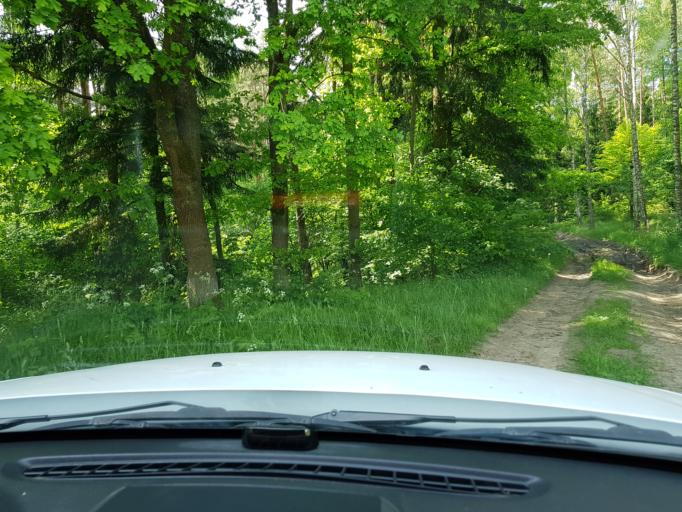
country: PL
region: West Pomeranian Voivodeship
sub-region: Powiat drawski
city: Drawsko Pomorskie
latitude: 53.5521
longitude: 15.7109
